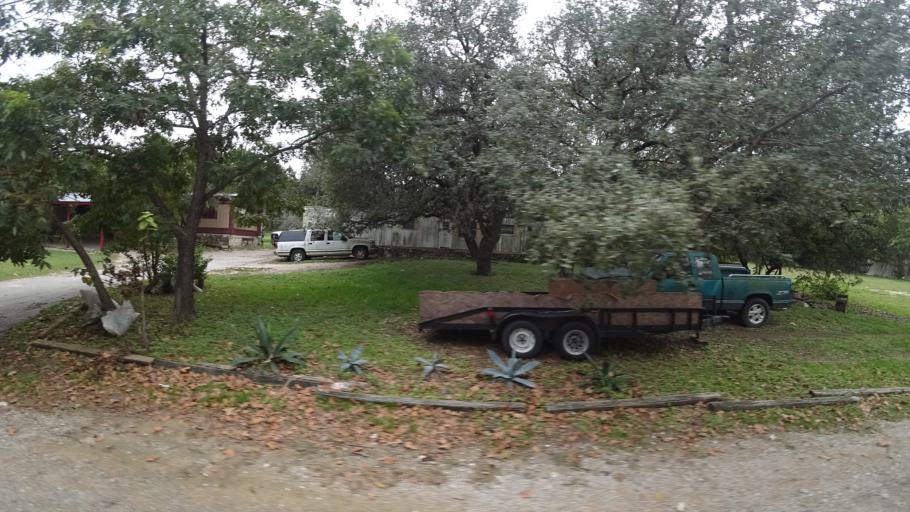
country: US
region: Texas
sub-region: Travis County
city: Hudson Bend
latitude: 30.3751
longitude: -97.9325
